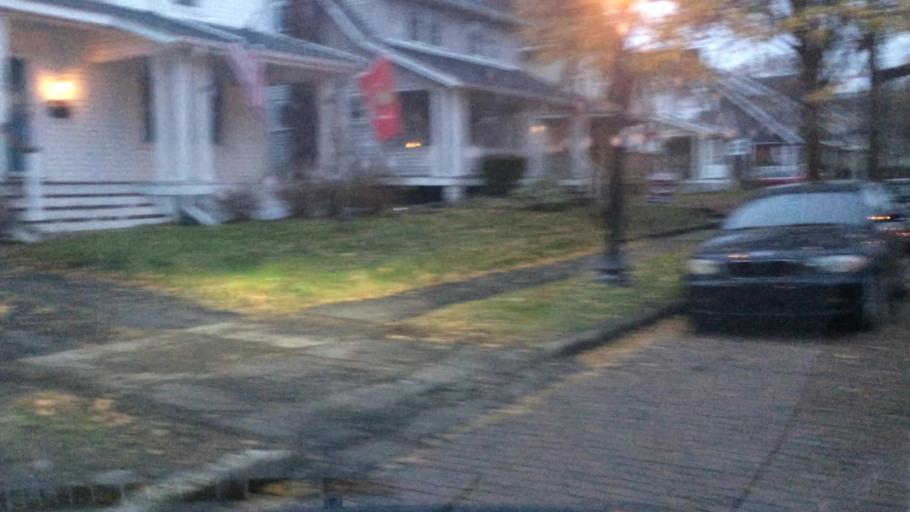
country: US
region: Ohio
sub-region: Summit County
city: Akron
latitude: 41.0463
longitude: -81.5091
